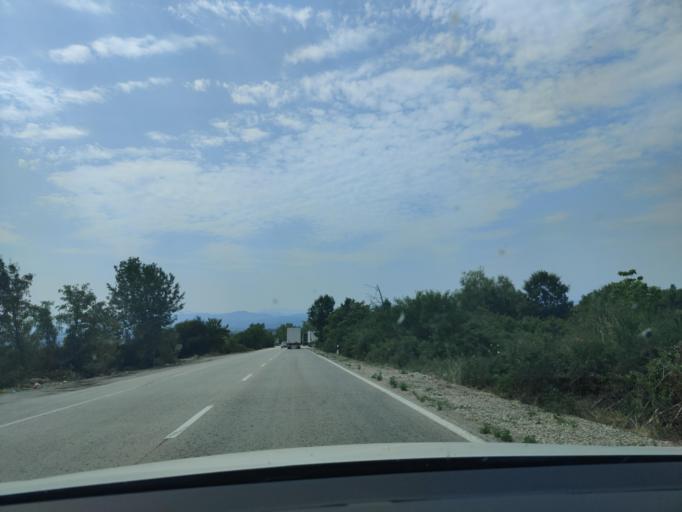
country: BG
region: Vidin
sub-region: Obshtina Dimovo
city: Dimovo
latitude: 43.7818
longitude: 22.7435
